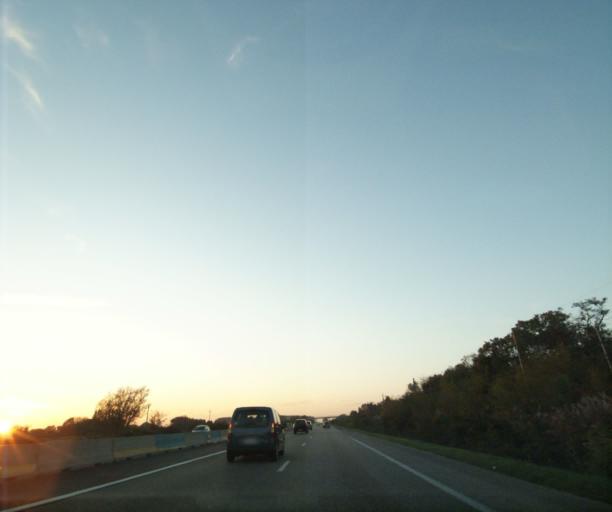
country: FR
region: Provence-Alpes-Cote d'Azur
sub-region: Departement des Bouches-du-Rhone
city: Arles
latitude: 43.6456
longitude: 4.6981
